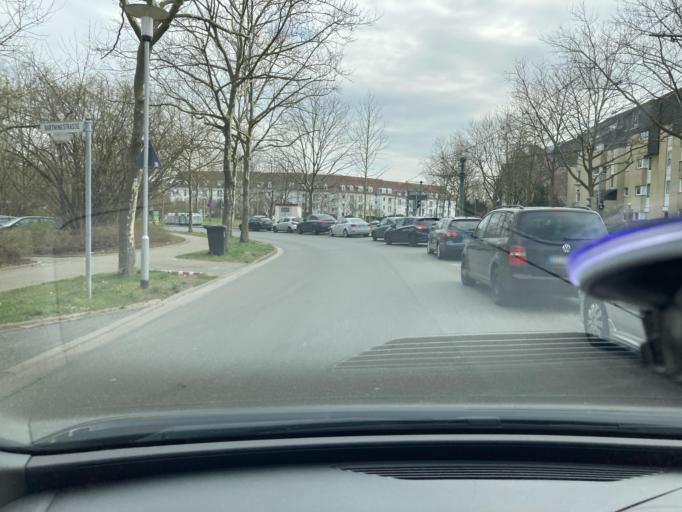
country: DE
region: Hesse
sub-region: Regierungsbezirk Darmstadt
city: Darmstadt
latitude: 49.9031
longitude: 8.6809
